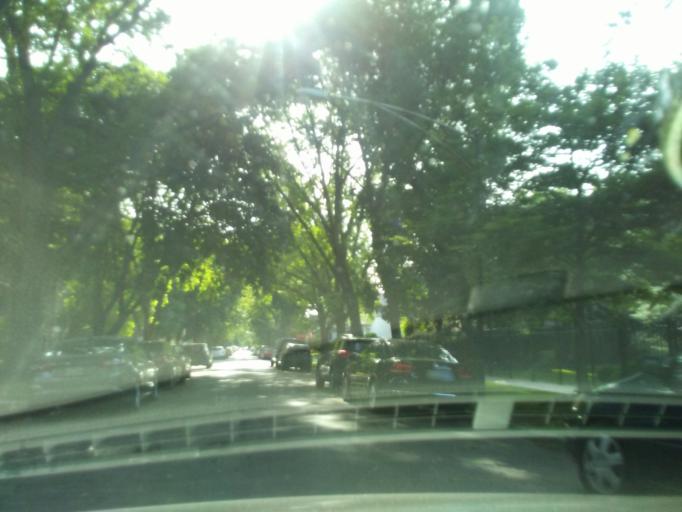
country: US
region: Illinois
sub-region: Cook County
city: Lincolnwood
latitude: 41.9779
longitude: -87.6812
